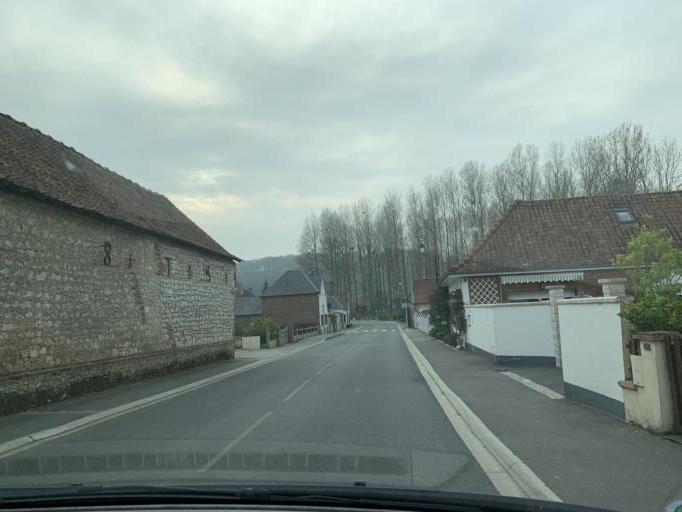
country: FR
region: Nord-Pas-de-Calais
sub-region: Departement du Pas-de-Calais
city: Montreuil
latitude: 50.4995
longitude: 1.7909
